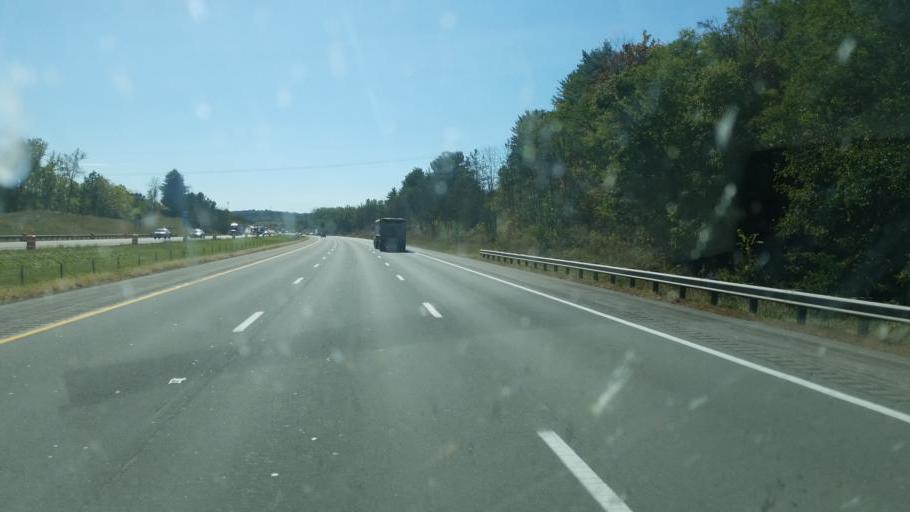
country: US
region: Ohio
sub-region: Richland County
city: Lincoln Heights
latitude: 40.7958
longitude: -82.3992
